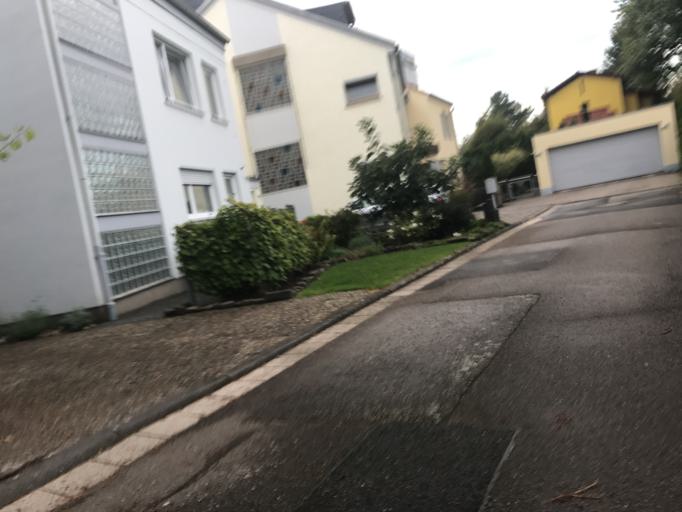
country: DE
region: Rheinland-Pfalz
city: Mainz
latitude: 49.9804
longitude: 8.2513
